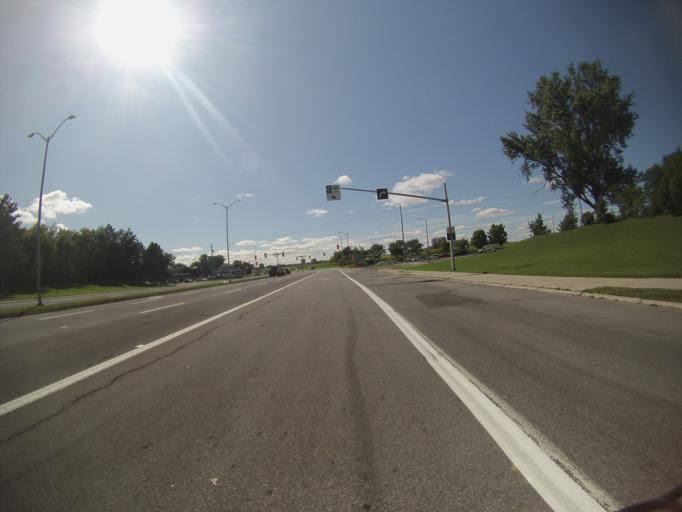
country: CA
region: Ontario
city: Ottawa
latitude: 45.3753
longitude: -75.7062
